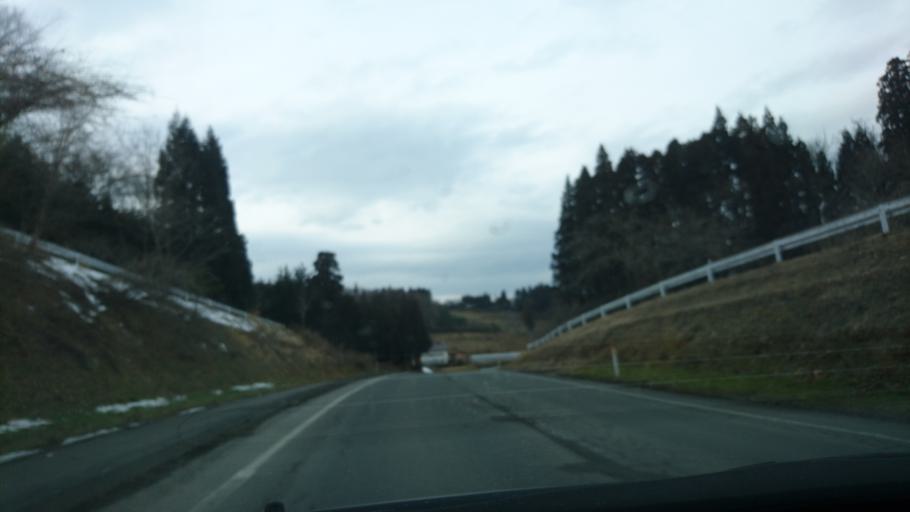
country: JP
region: Iwate
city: Ichinoseki
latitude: 38.9622
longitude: 141.3649
